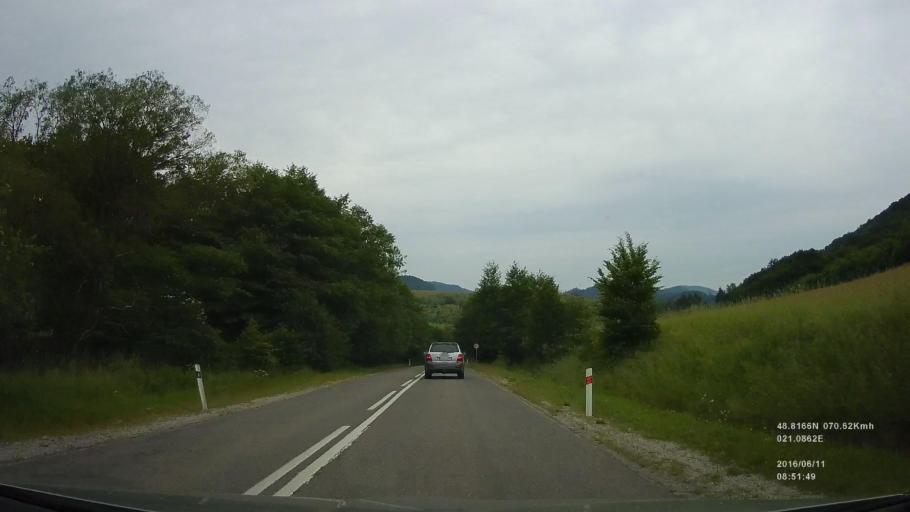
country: SK
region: Kosicky
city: Gelnica
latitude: 48.8126
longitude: 21.0938
